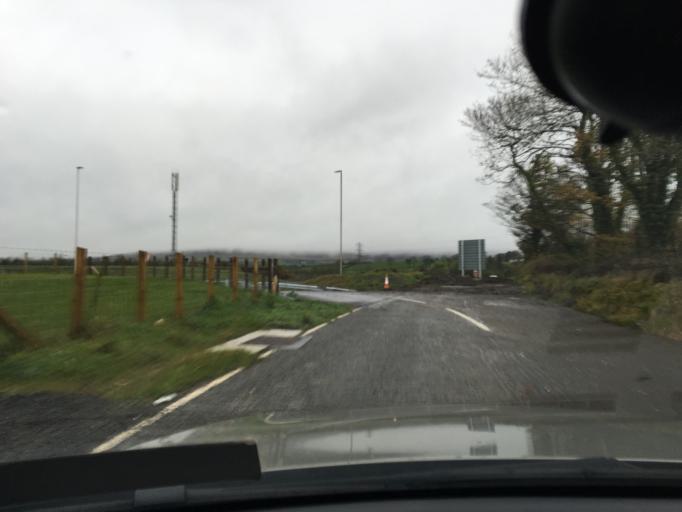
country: GB
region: Northern Ireland
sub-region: Larne District
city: Larne
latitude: 54.8339
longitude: -5.8740
